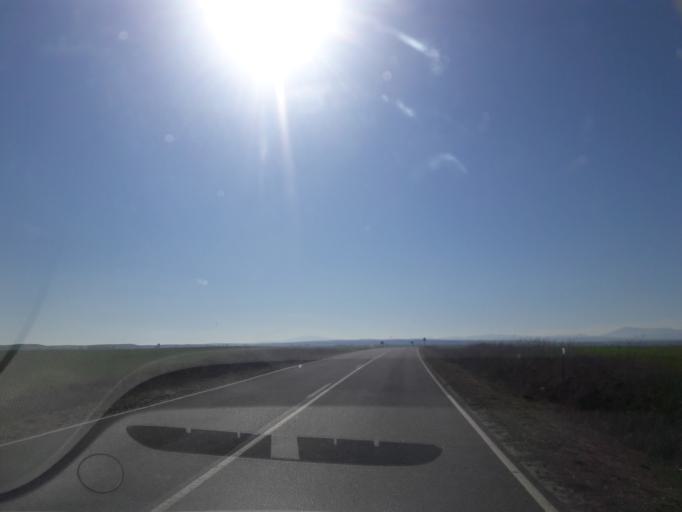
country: ES
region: Castille and Leon
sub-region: Provincia de Salamanca
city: Santiago de la Puebla
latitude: 40.8124
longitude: -5.2544
